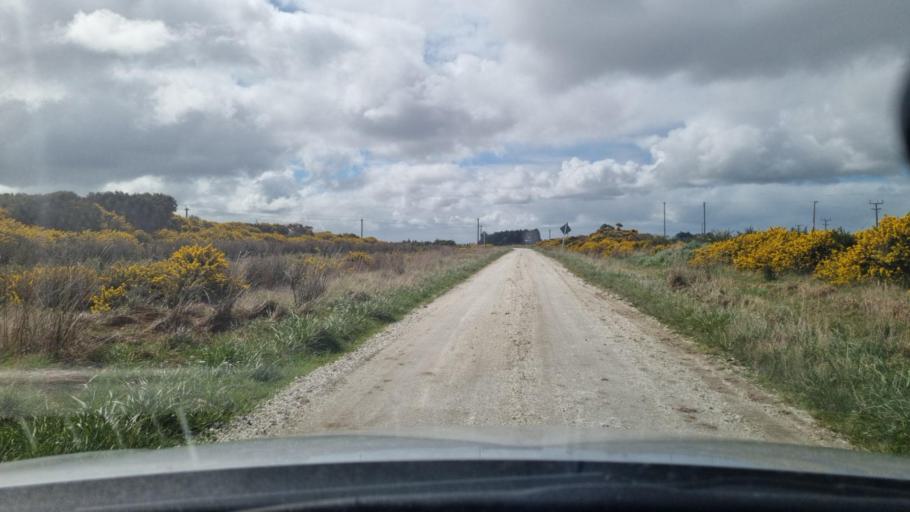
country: NZ
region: Southland
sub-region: Invercargill City
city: Bluff
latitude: -46.5275
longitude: 168.3070
